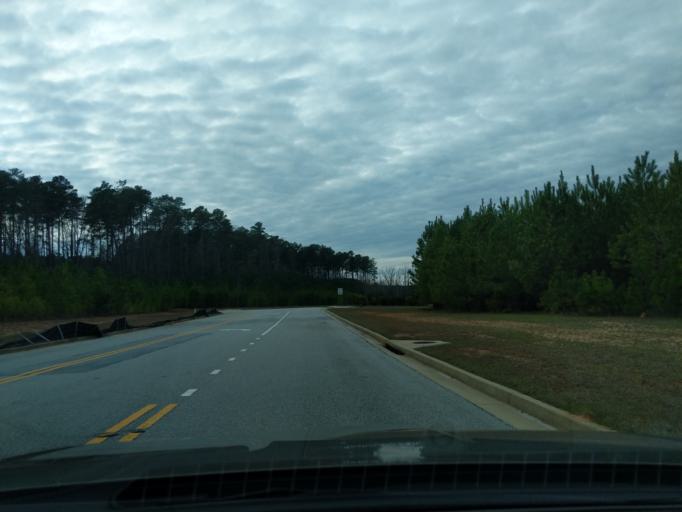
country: US
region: Georgia
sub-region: Columbia County
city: Grovetown
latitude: 33.4765
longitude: -82.1890
